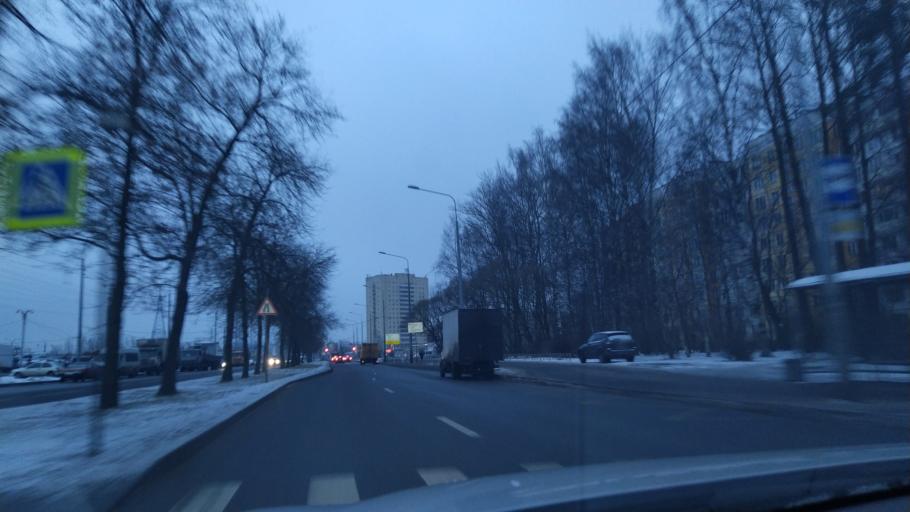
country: RU
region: St.-Petersburg
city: Grazhdanka
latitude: 60.0164
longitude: 30.4282
